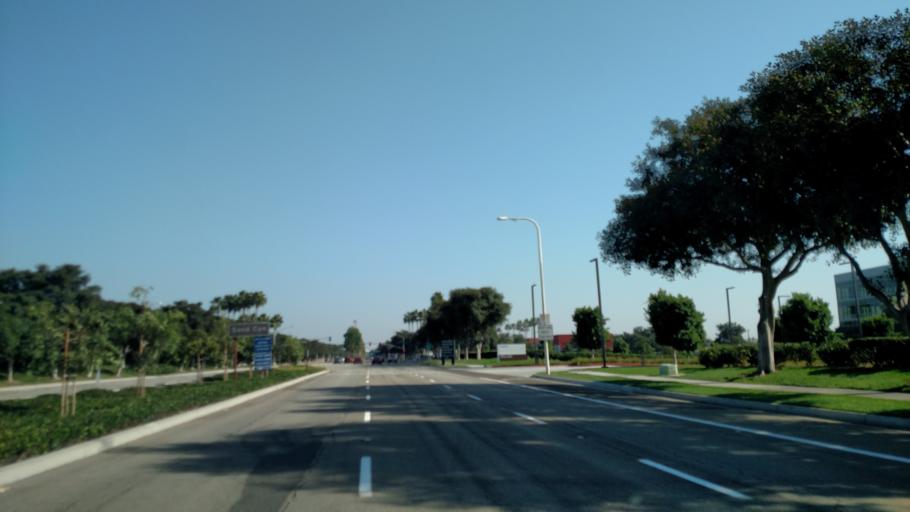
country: US
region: California
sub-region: Orange County
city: Irvine
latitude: 33.6716
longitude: -117.7675
